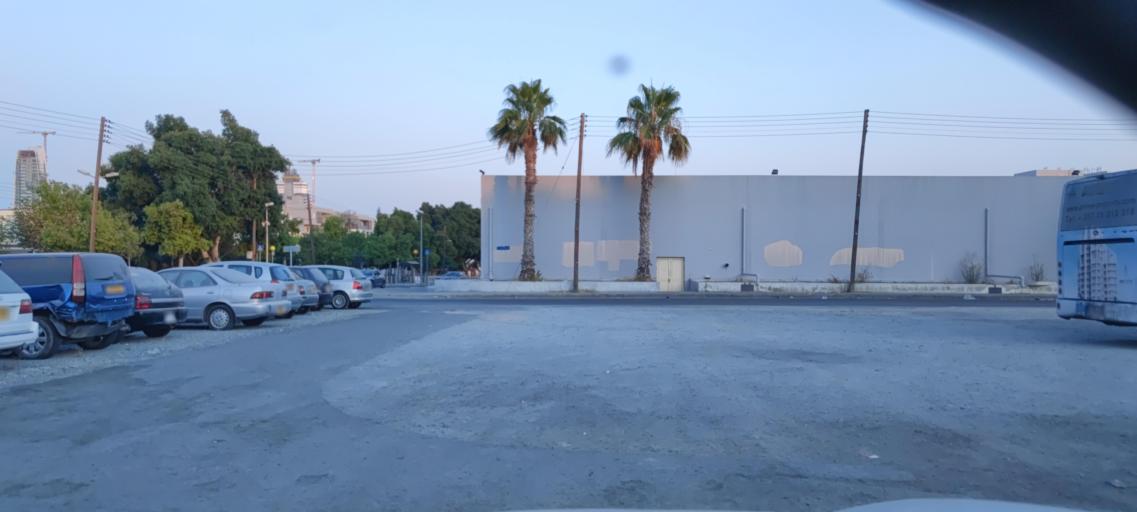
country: CY
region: Limassol
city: Limassol
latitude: 34.6925
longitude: 33.0523
